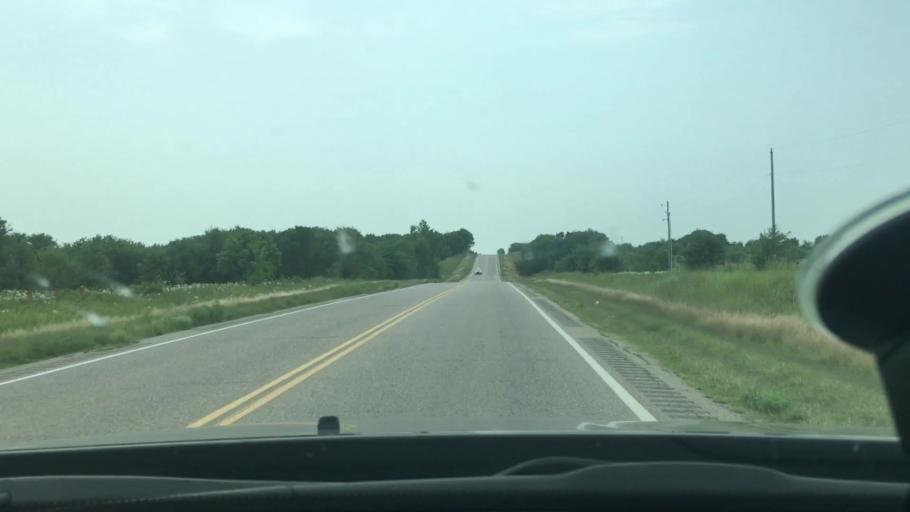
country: US
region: Oklahoma
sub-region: Marshall County
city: Madill
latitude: 34.0578
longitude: -96.7611
